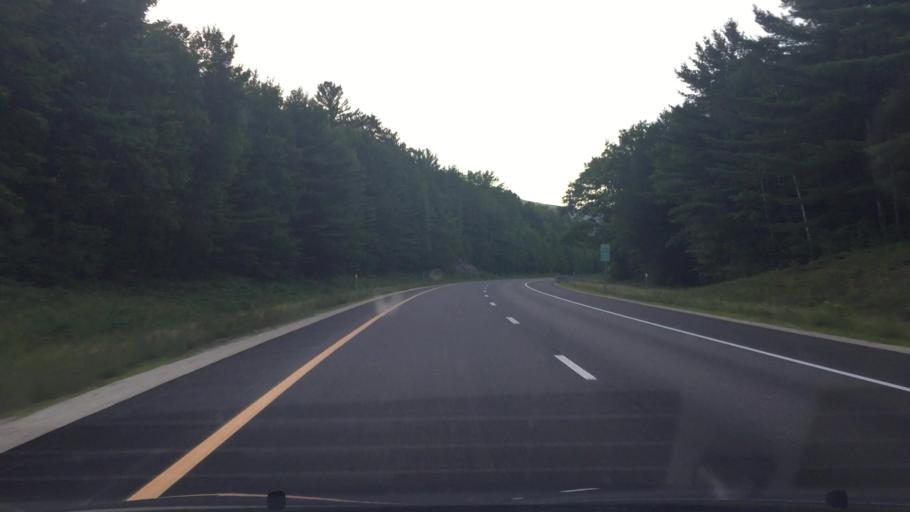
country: US
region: New Hampshire
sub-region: Grafton County
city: Thornton
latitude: 43.8983
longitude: -71.6874
